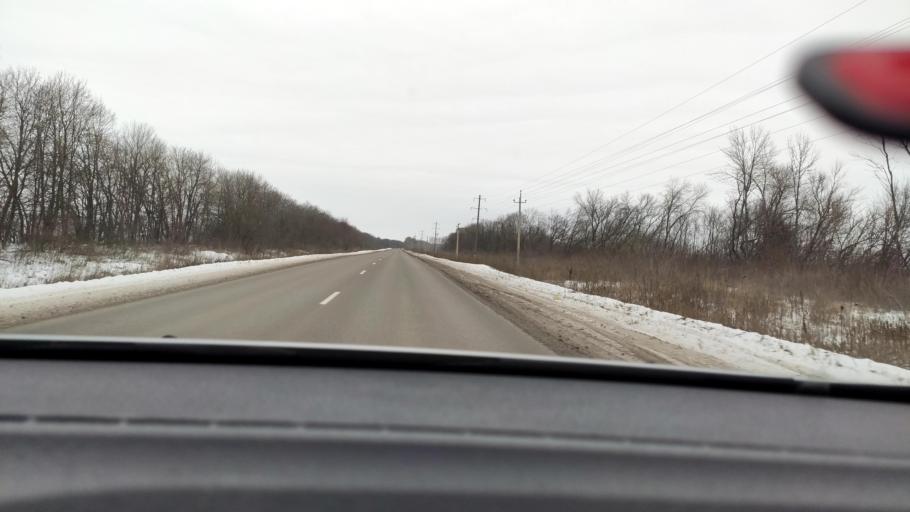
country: RU
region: Voronezj
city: Latnaya
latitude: 51.7600
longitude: 38.9156
